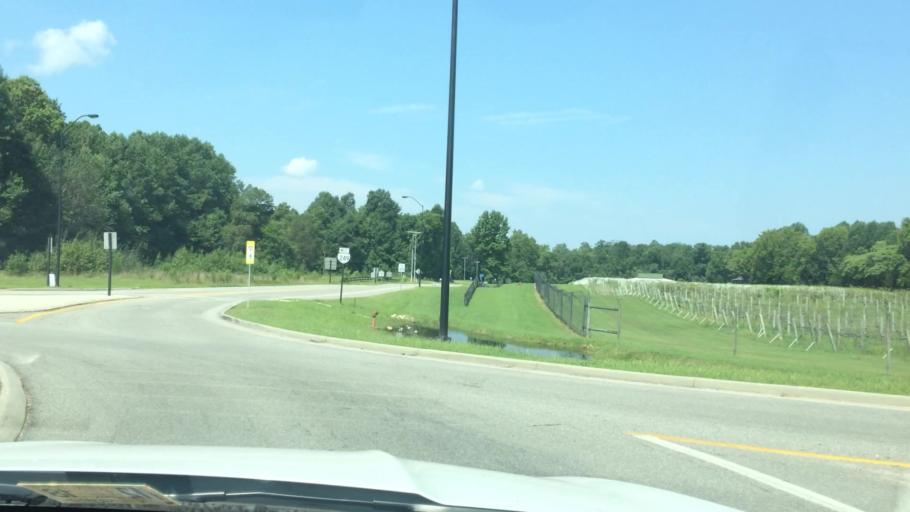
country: US
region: Virginia
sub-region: New Kent County
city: New Kent
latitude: 37.5248
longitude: -77.0755
